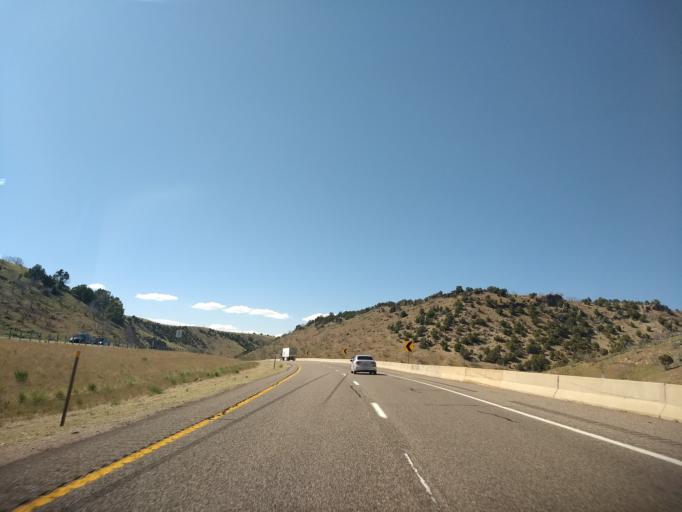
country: US
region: Utah
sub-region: Millard County
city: Fillmore
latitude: 38.6807
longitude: -112.5957
